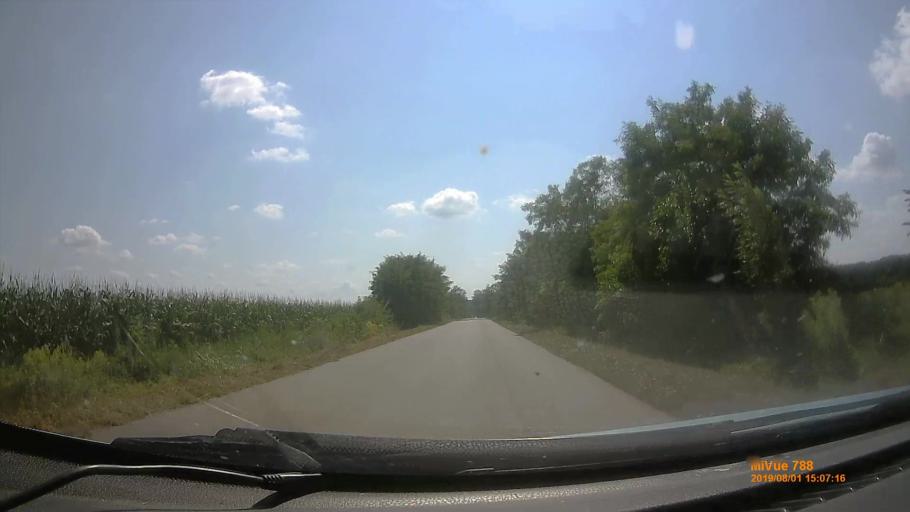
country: HU
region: Baranya
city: Sellye
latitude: 45.8602
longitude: 17.8316
